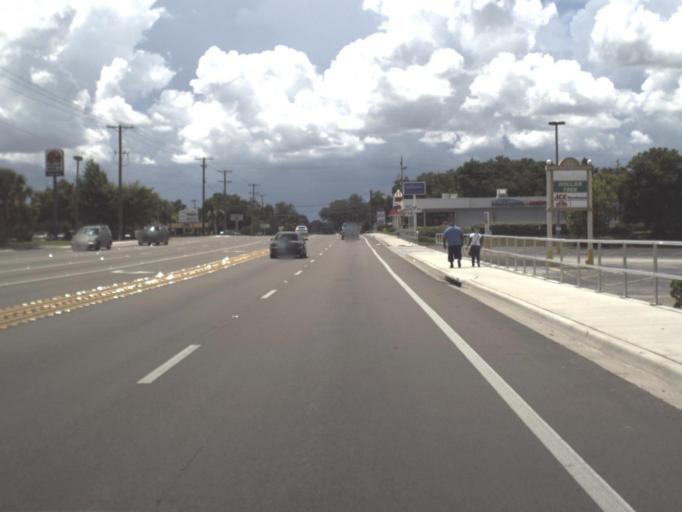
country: US
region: Florida
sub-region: Hillsborough County
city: Seffner
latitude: 27.9817
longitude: -82.2863
